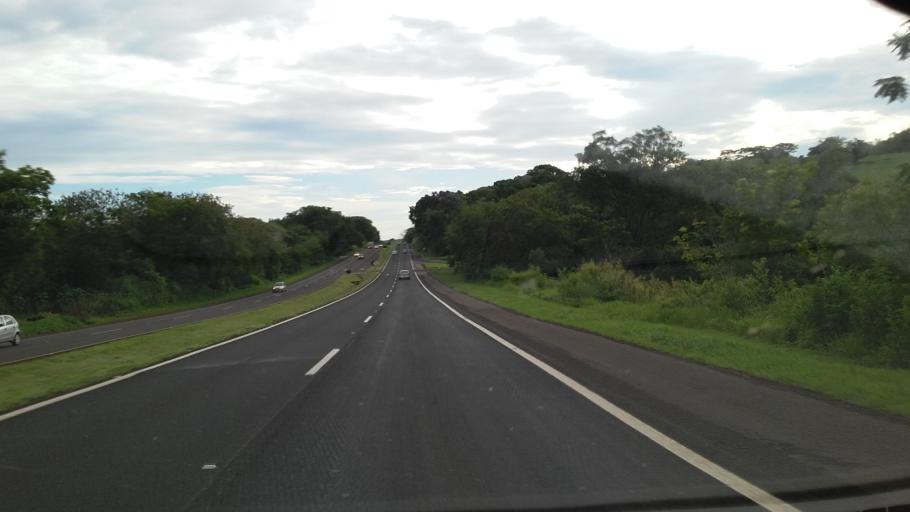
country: BR
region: Parana
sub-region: Paicandu
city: Paicandu
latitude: -23.5032
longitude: -52.0191
